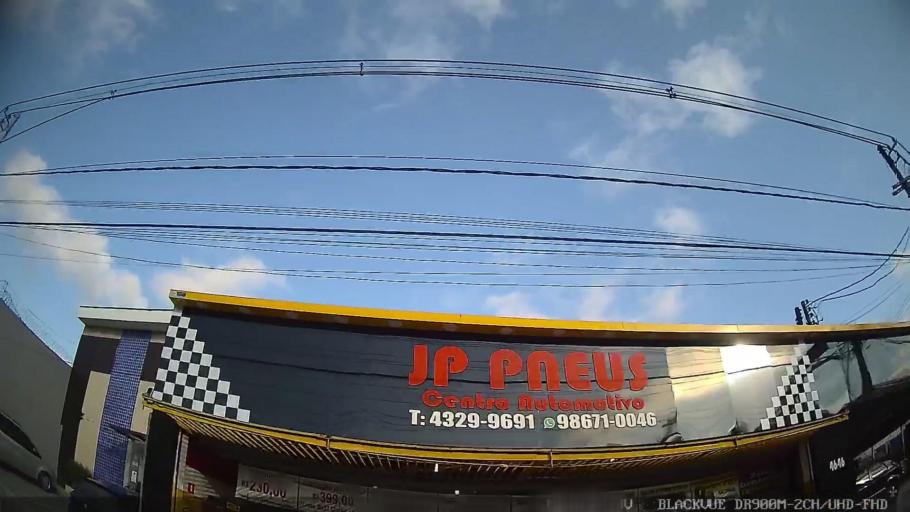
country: BR
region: Sao Paulo
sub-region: Taboao Da Serra
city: Taboao da Serra
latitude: -23.6241
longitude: -46.7643
